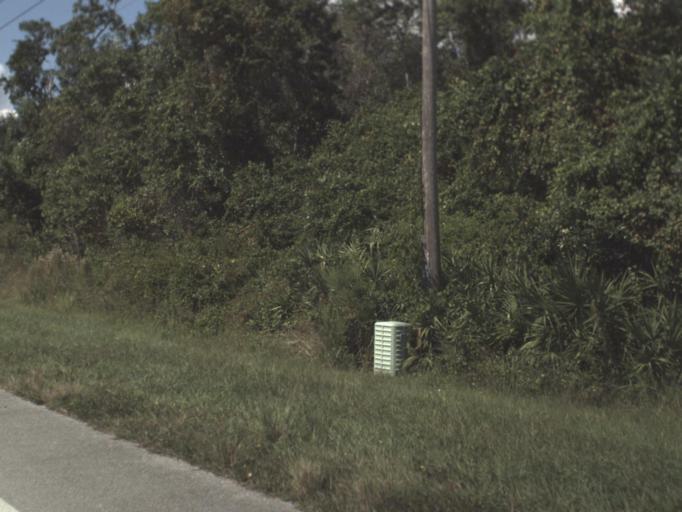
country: US
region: Florida
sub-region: Highlands County
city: Sebring
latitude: 27.4284
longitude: -81.3979
